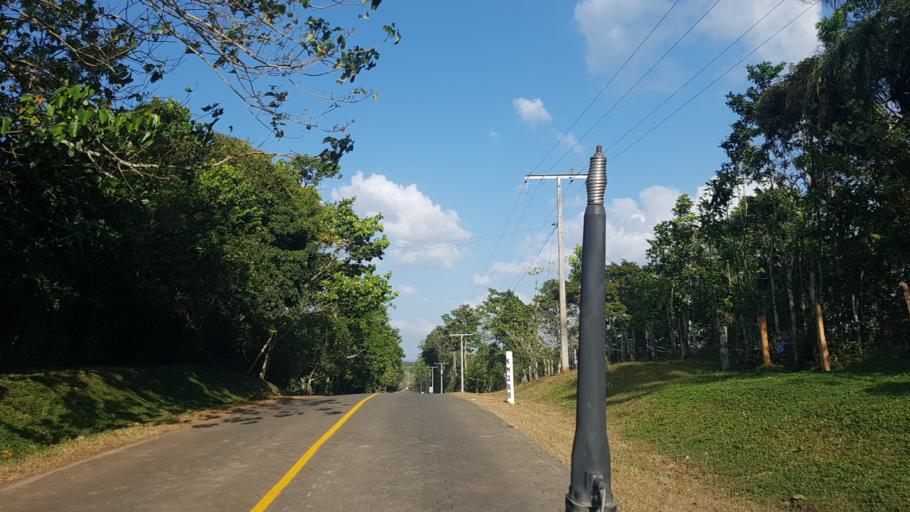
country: NI
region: Atlantico Sur
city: Nueva Guinea
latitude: 11.6892
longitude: -84.4275
